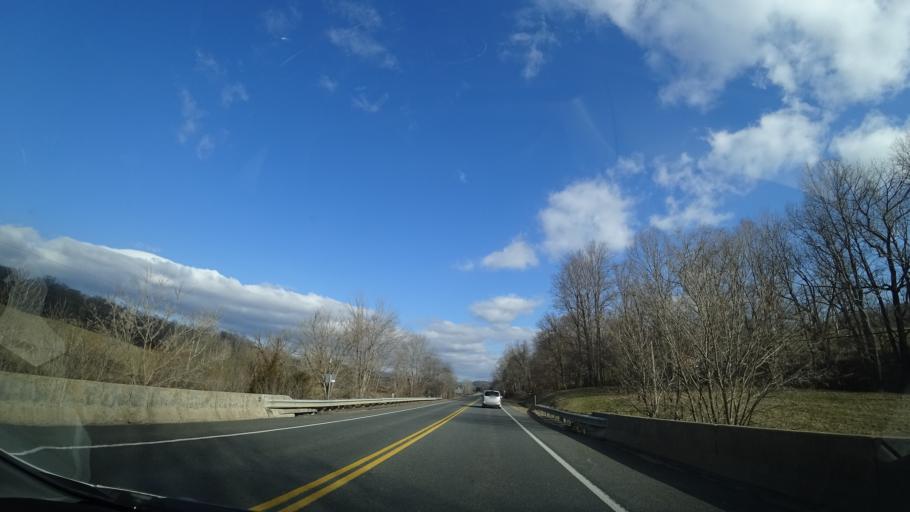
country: US
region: Virginia
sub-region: Fauquier County
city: Marshall
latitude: 38.9340
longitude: -77.9332
